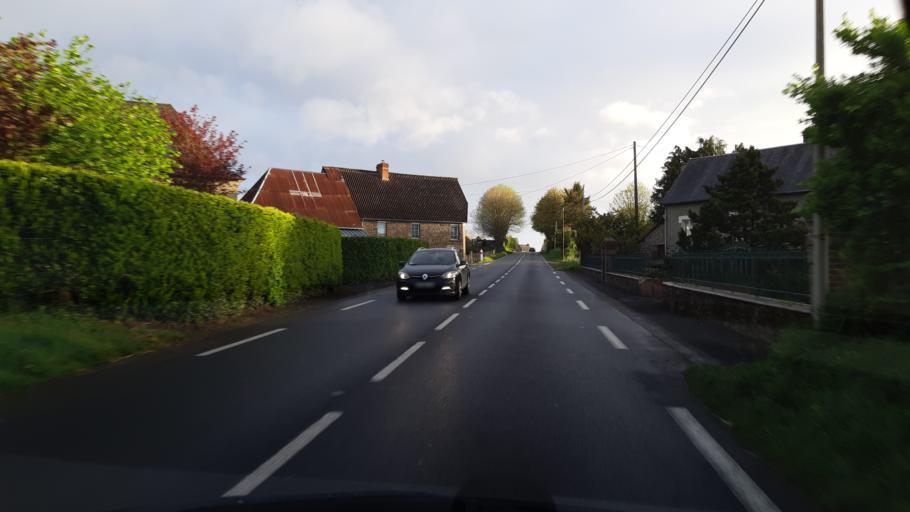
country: FR
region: Lower Normandy
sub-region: Departement de la Manche
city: Tessy-sur-Vire
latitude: 49.0244
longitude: -1.1457
